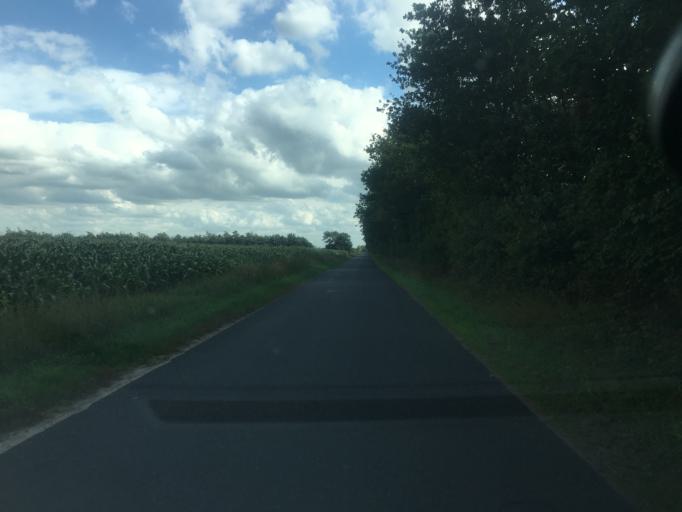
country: DK
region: South Denmark
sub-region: Tonder Kommune
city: Logumkloster
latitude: 55.0105
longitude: 9.0036
